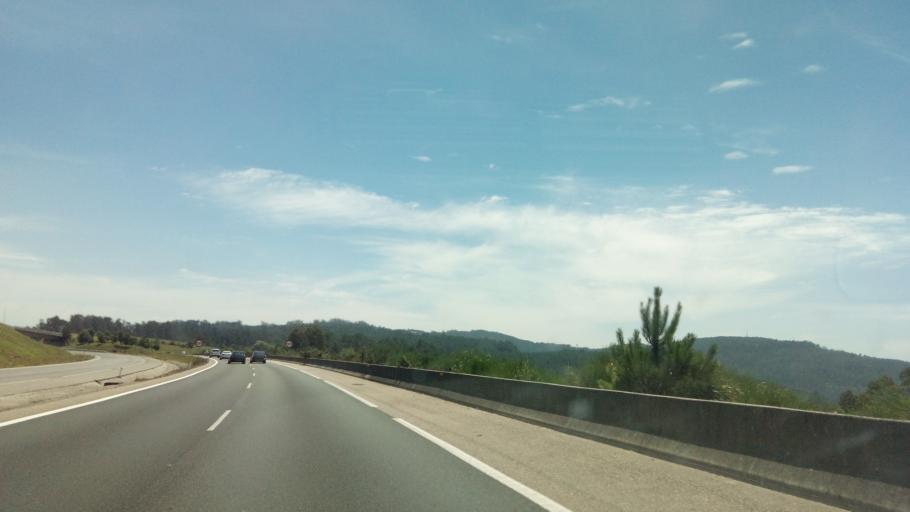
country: ES
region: Galicia
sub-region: Provincia de Pontevedra
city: Vigo
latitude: 42.2017
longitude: -8.6688
